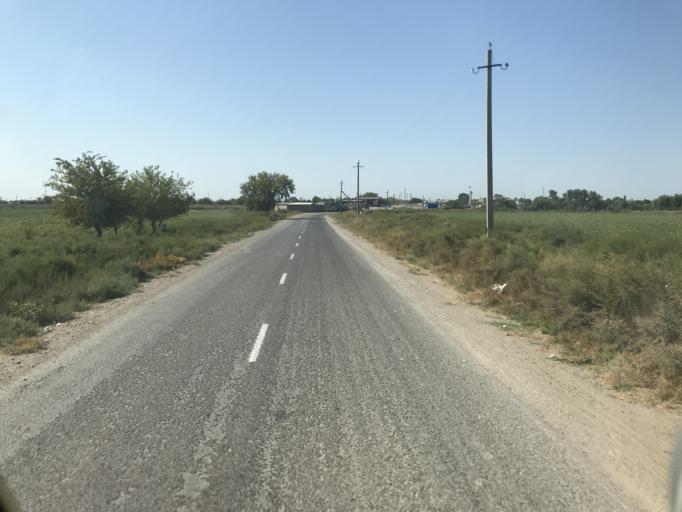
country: KZ
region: Ongtustik Qazaqstan
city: Myrzakent
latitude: 40.6726
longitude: 68.5532
